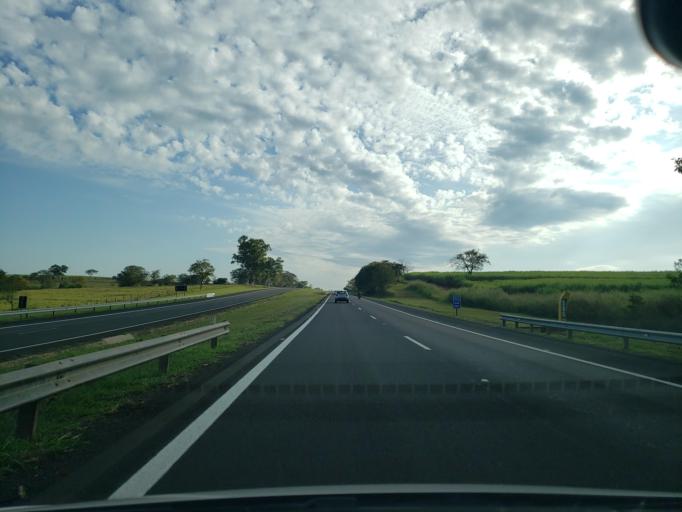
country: BR
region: Sao Paulo
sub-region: Guararapes
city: Guararapes
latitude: -21.2005
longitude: -50.5776
